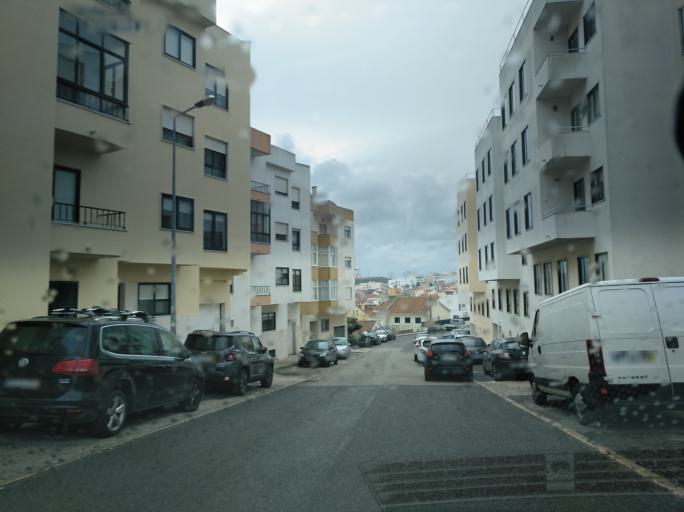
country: PT
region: Lisbon
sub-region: Odivelas
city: Famoes
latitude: 38.7955
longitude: -9.2188
